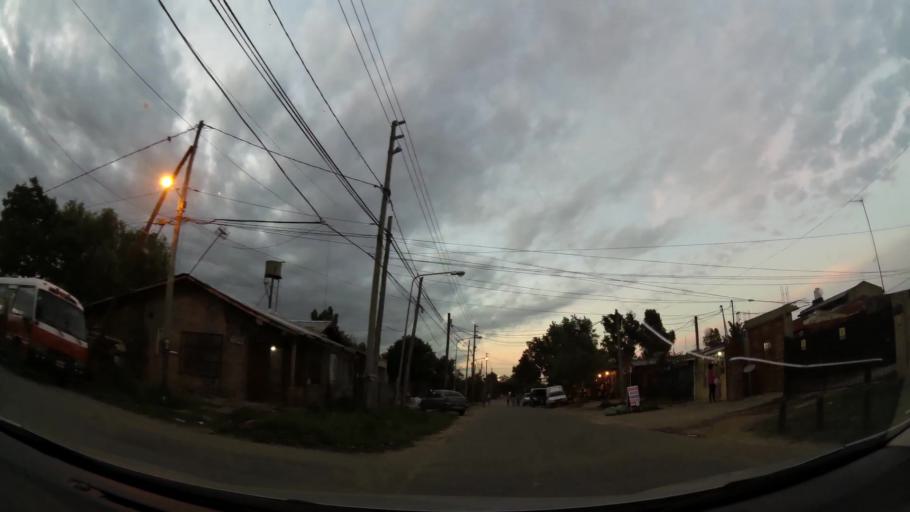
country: AR
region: Buenos Aires
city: Santa Catalina - Dique Lujan
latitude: -34.4164
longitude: -58.6840
